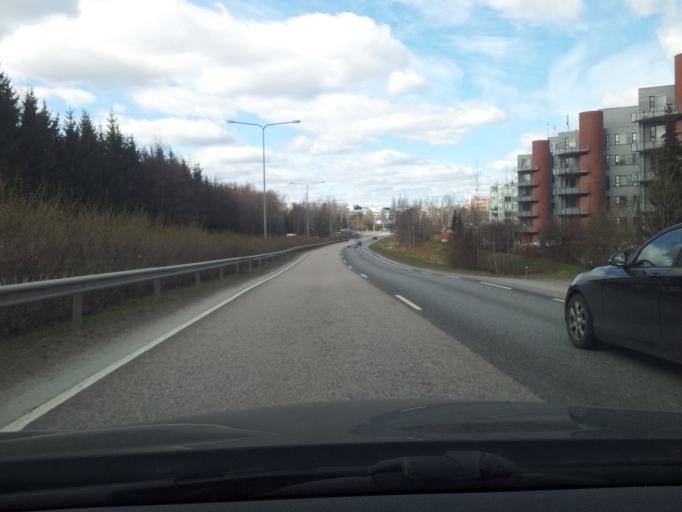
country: FI
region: Uusimaa
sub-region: Helsinki
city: Otaniemi
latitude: 60.1830
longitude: 24.8142
